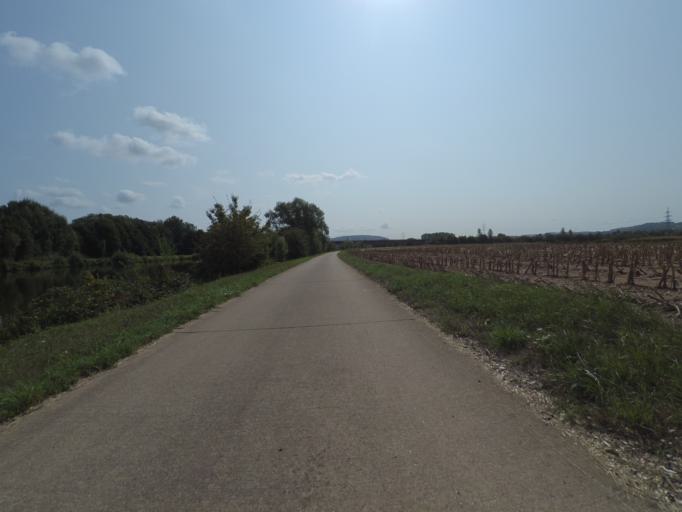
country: DE
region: Saarland
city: Mettlach
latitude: 49.4657
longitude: 6.6103
